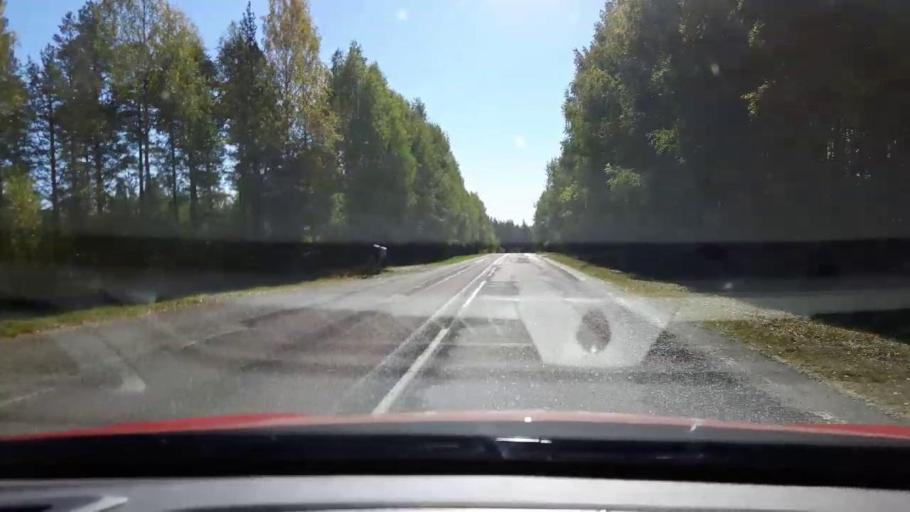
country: SE
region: Jaemtland
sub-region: Harjedalens Kommun
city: Sveg
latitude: 62.1244
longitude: 14.1645
